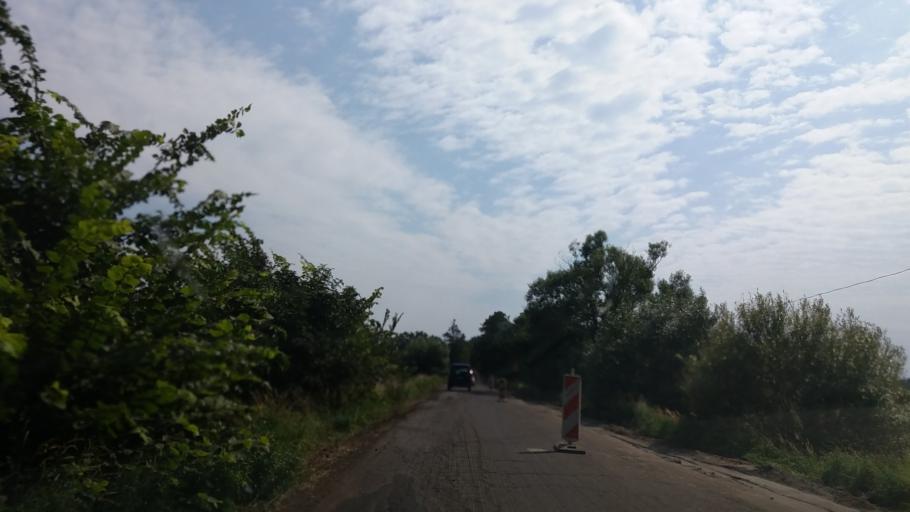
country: PL
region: Lubusz
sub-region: Powiat strzelecko-drezdenecki
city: Stare Kurowo
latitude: 52.7700
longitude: 15.6441
